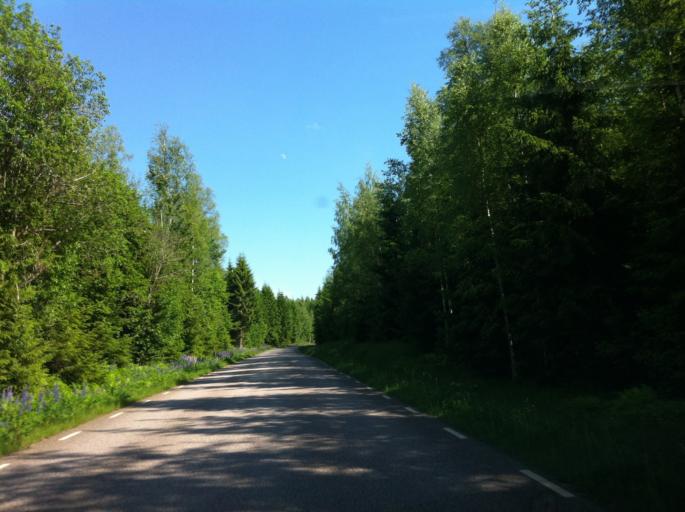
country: SE
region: Vaermland
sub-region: Sunne Kommun
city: Sunne
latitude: 59.7328
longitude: 13.2106
